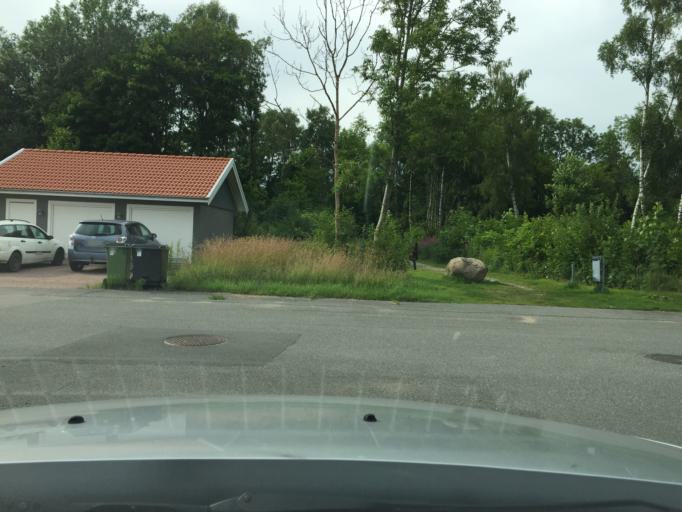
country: SE
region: Skane
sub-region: Hassleholms Kommun
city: Sosdala
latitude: 56.0367
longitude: 13.6756
